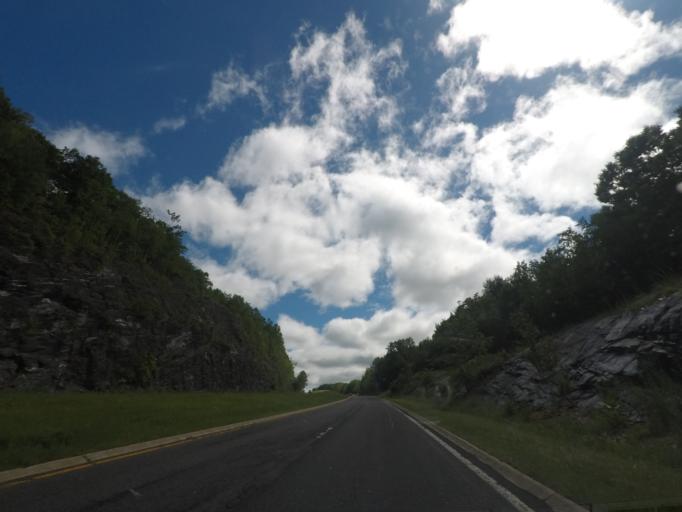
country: US
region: New York
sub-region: Columbia County
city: Chatham
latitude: 42.3246
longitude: -73.5744
